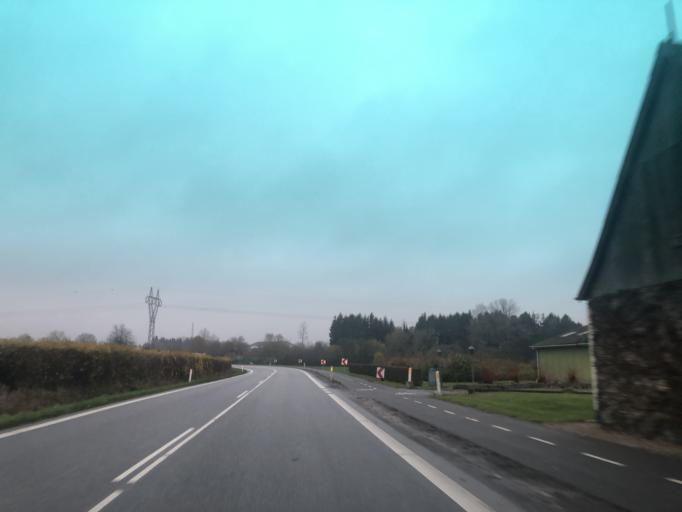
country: DK
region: South Denmark
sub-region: Nyborg Kommune
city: Ullerslev
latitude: 55.2719
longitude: 10.6781
